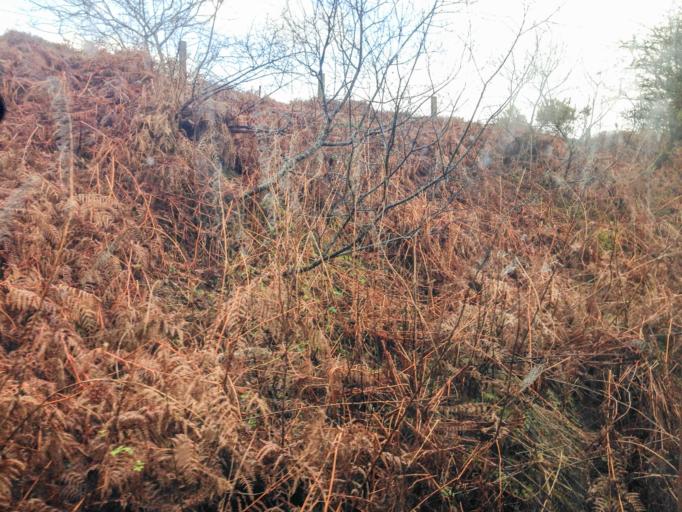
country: GB
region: Scotland
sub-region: Highland
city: Fort William
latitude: 56.8449
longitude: -5.1000
